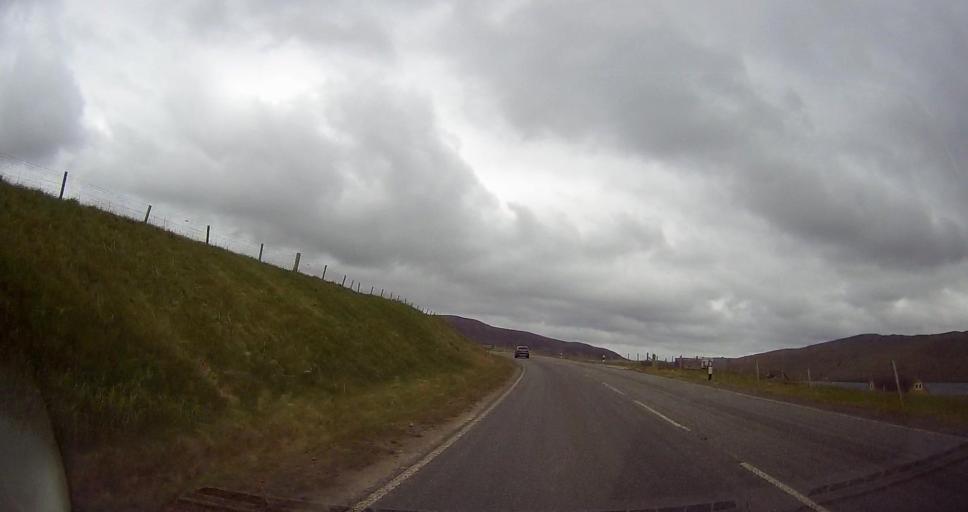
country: GB
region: Scotland
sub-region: Shetland Islands
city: Lerwick
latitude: 60.3712
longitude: -1.3322
